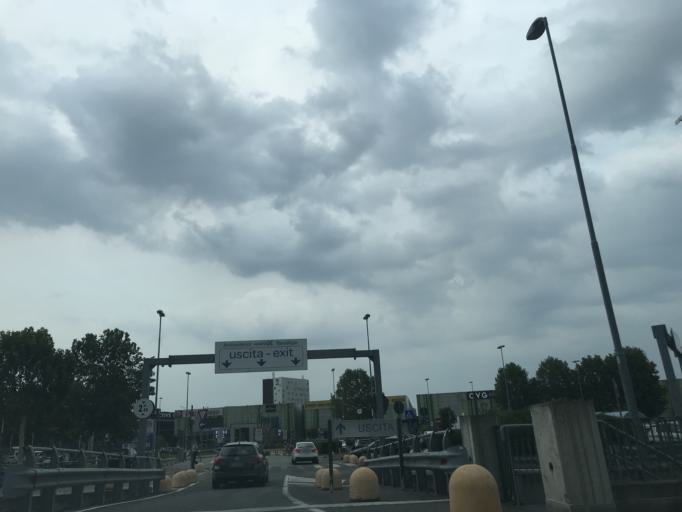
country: IT
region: Lombardy
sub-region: Citta metropolitana di Milano
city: Rozzano
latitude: 45.4045
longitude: 9.1512
